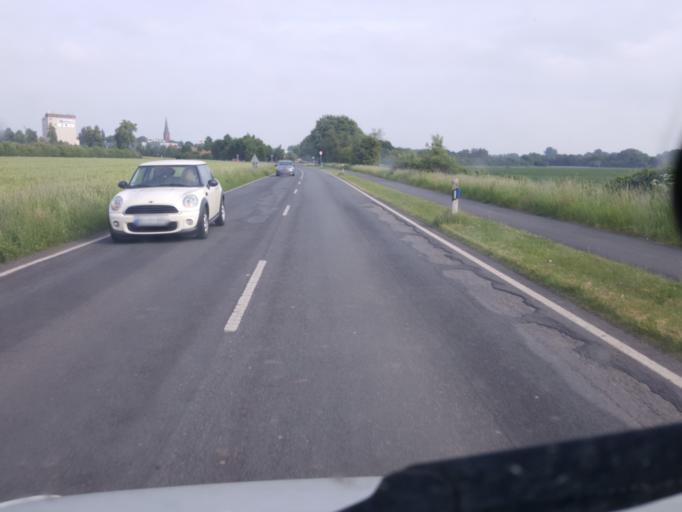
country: DE
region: Lower Saxony
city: Nienburg
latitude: 52.6473
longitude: 9.1939
